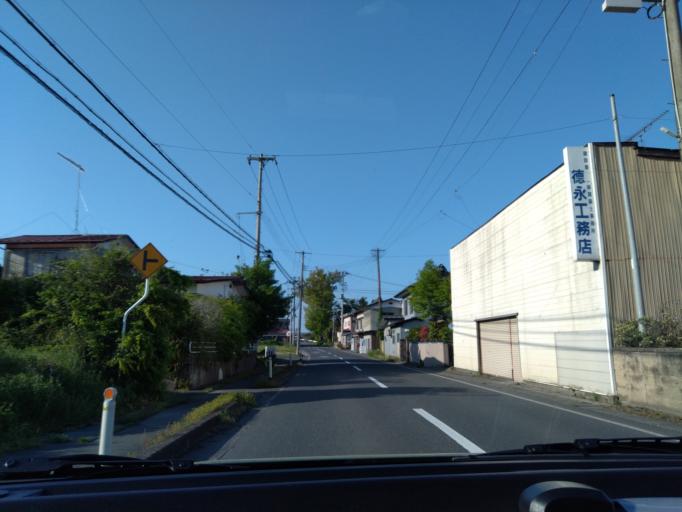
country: JP
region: Iwate
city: Ichinoseki
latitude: 38.7963
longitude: 141.1739
